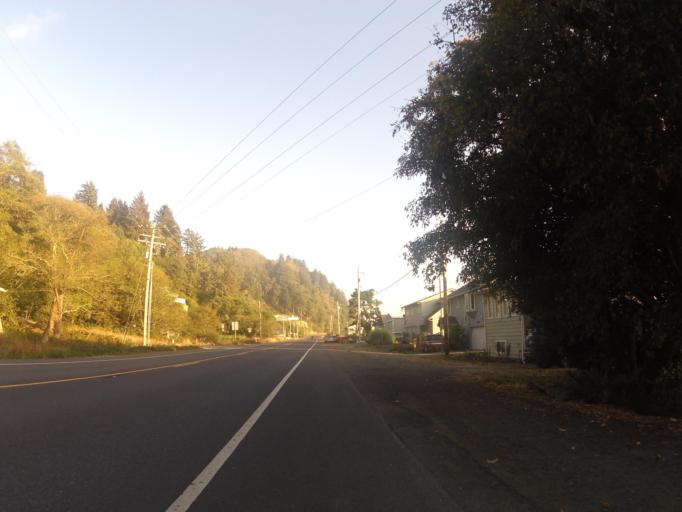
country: US
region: Oregon
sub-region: Tillamook County
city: Rockaway Beach
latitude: 45.5666
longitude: -123.9395
